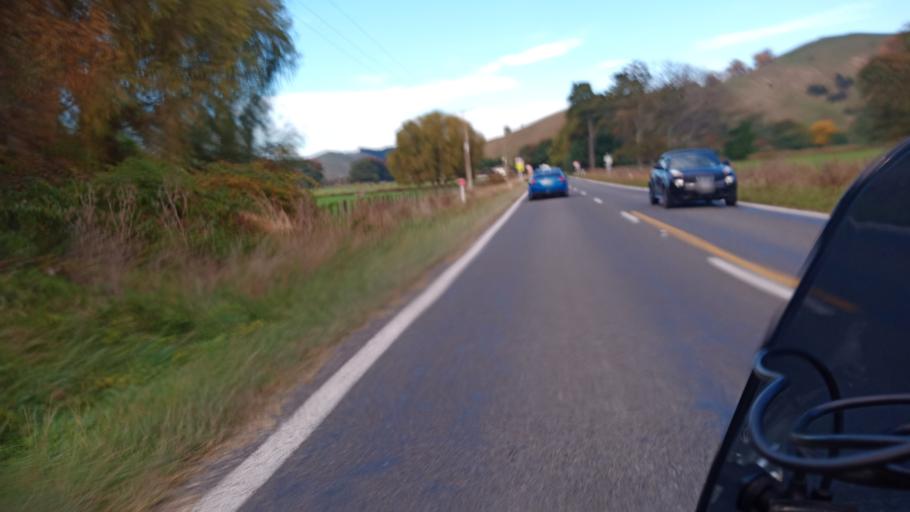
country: NZ
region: Gisborne
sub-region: Gisborne District
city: Gisborne
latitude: -38.7569
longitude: 177.9203
